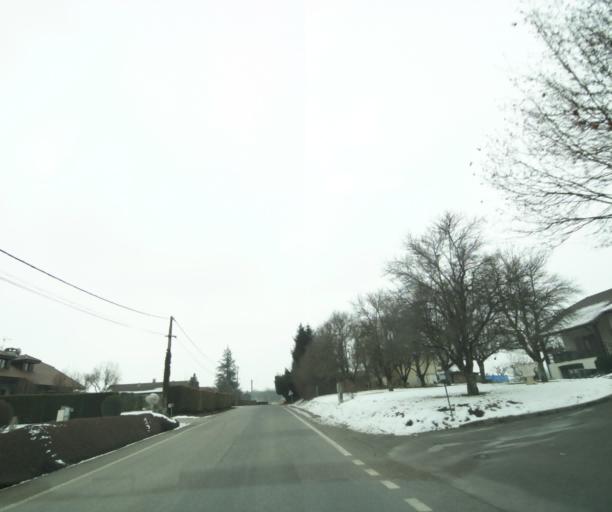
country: FR
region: Rhone-Alpes
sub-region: Departement de la Haute-Savoie
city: Reignier-Esery
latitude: 46.1317
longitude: 6.2800
